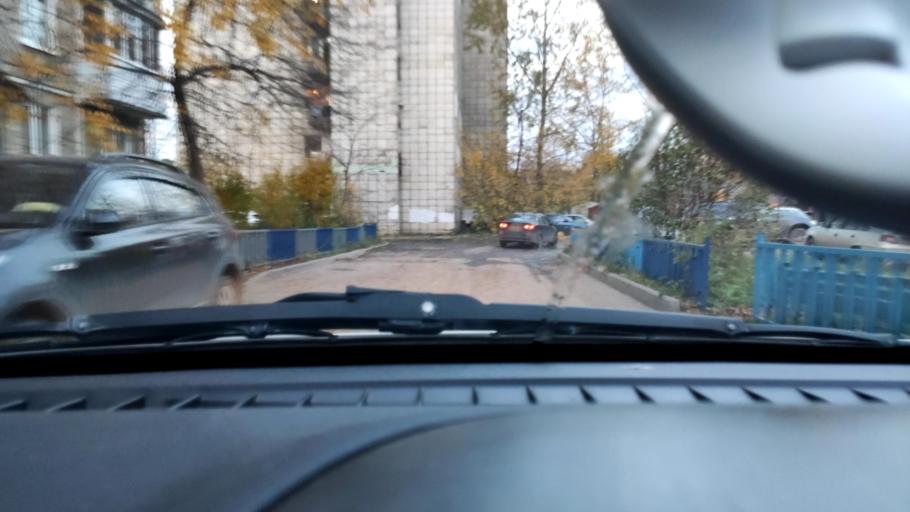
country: RU
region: Perm
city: Kondratovo
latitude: 57.9936
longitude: 56.1507
